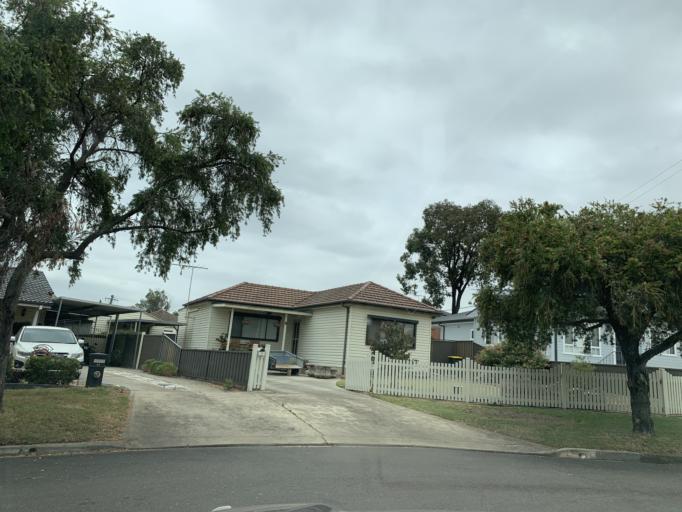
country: AU
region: New South Wales
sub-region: Blacktown
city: Blacktown
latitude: -33.7792
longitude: 150.8974
